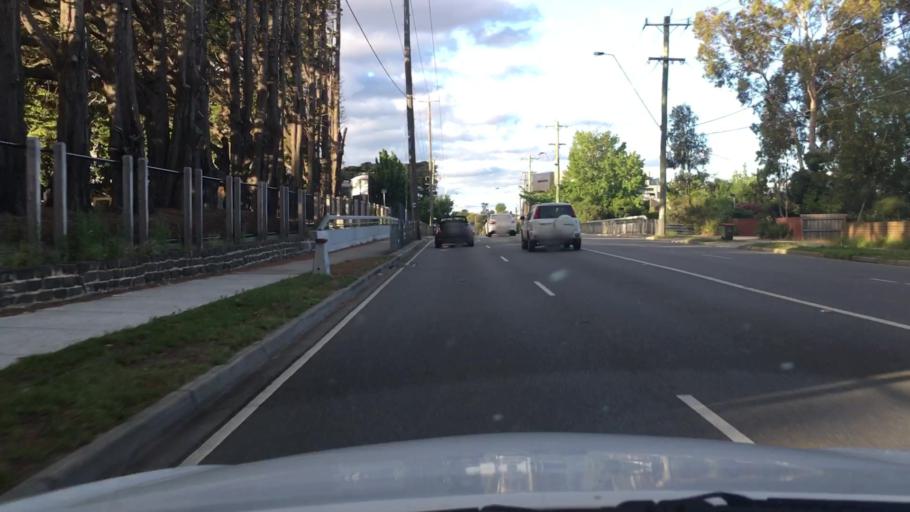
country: AU
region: Victoria
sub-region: Whitehorse
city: Box Hill
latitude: -37.8221
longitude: 145.1379
